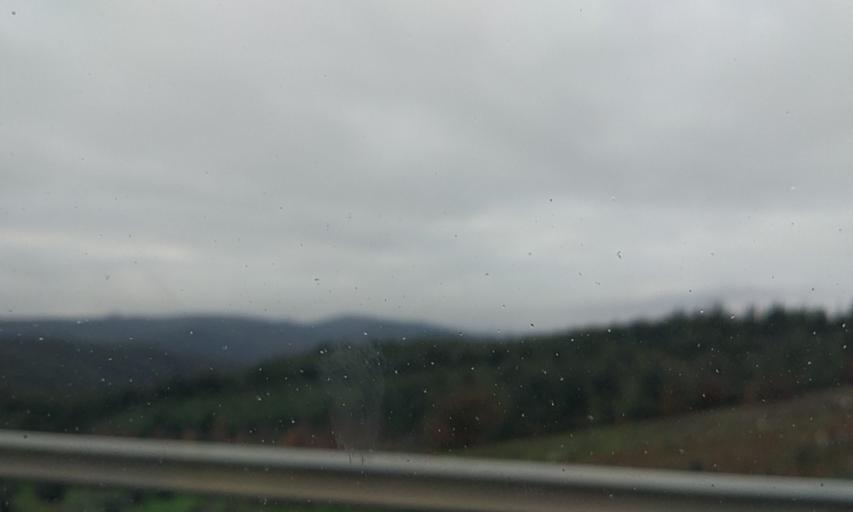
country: PT
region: Viseu
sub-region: Mortagua
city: Mortagua
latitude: 40.3674
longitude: -8.1943
